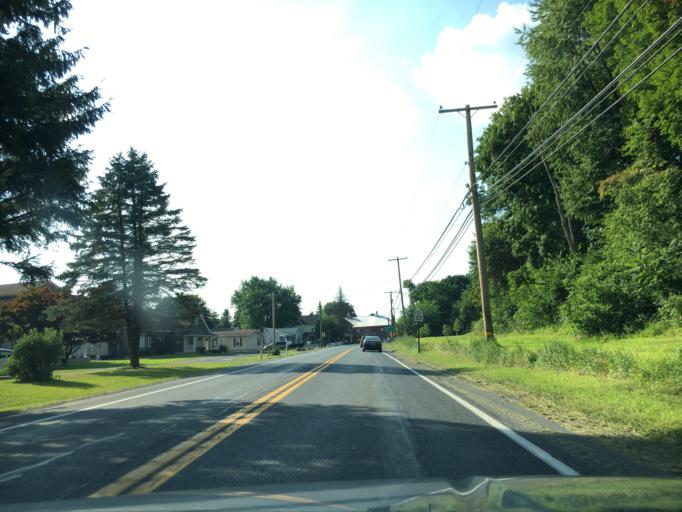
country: US
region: Pennsylvania
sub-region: Lehigh County
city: Egypt
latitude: 40.6626
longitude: -75.5623
